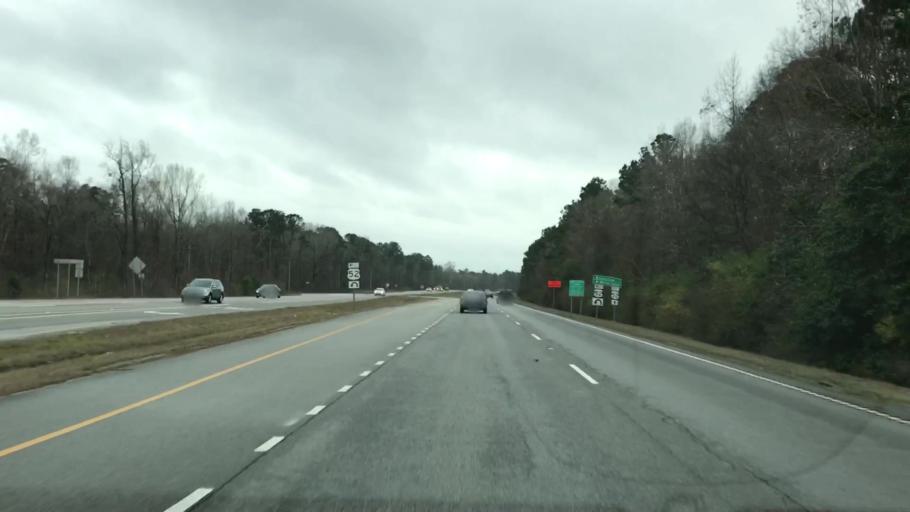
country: US
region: South Carolina
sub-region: Berkeley County
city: Moncks Corner
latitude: 33.1251
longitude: -80.0294
